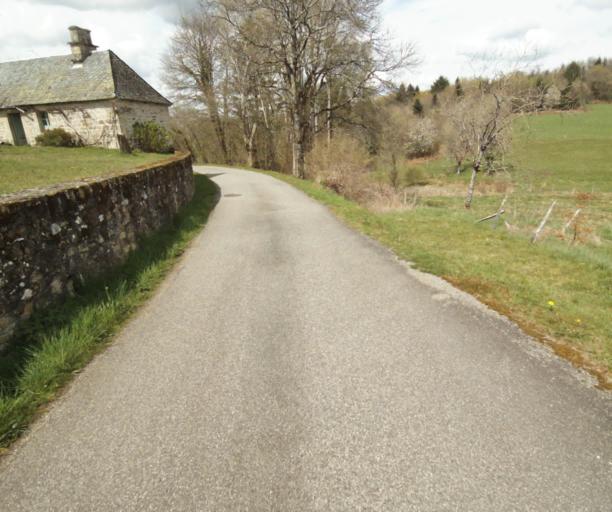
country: FR
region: Limousin
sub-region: Departement de la Correze
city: Laguenne
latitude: 45.1981
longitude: 1.8837
